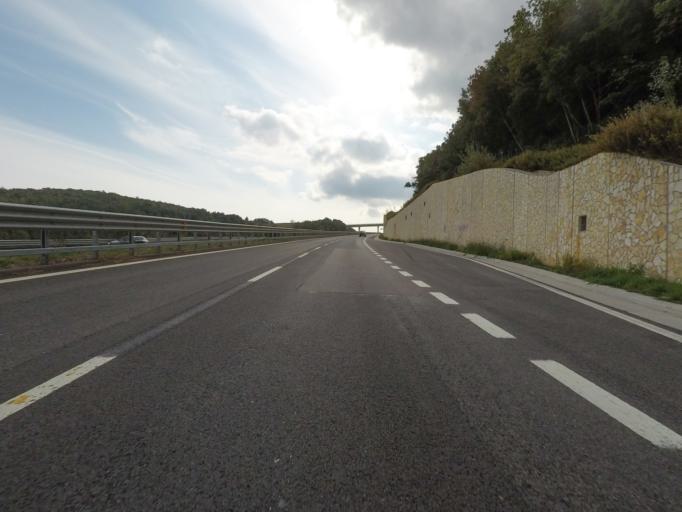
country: IT
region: Tuscany
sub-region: Provincia di Siena
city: Murlo
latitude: 43.1038
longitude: 11.2980
